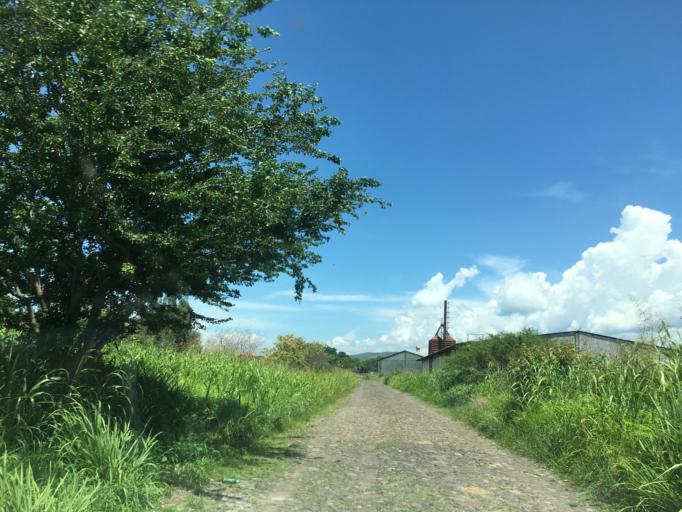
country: MX
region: Nayarit
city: Ixtlan del Rio
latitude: 21.0369
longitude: -104.3465
